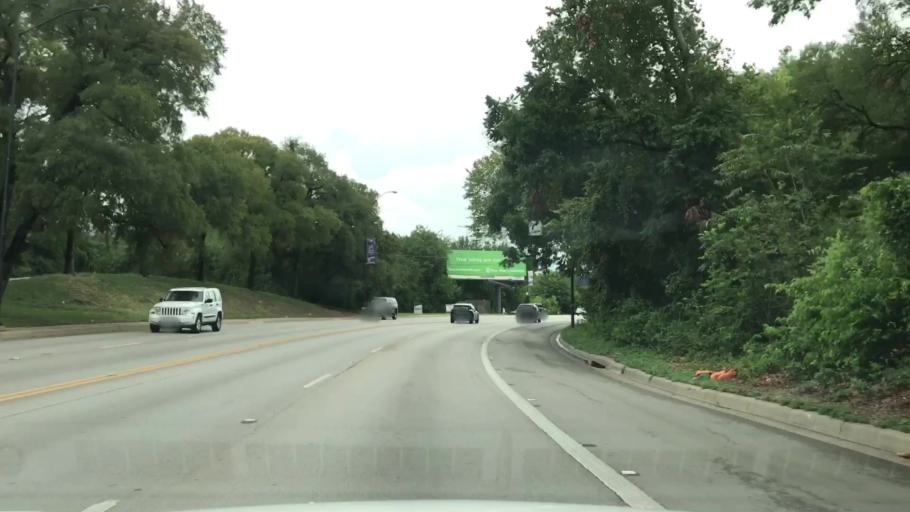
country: US
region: Texas
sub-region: Tarrant County
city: Fort Worth
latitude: 32.7182
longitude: -97.3608
